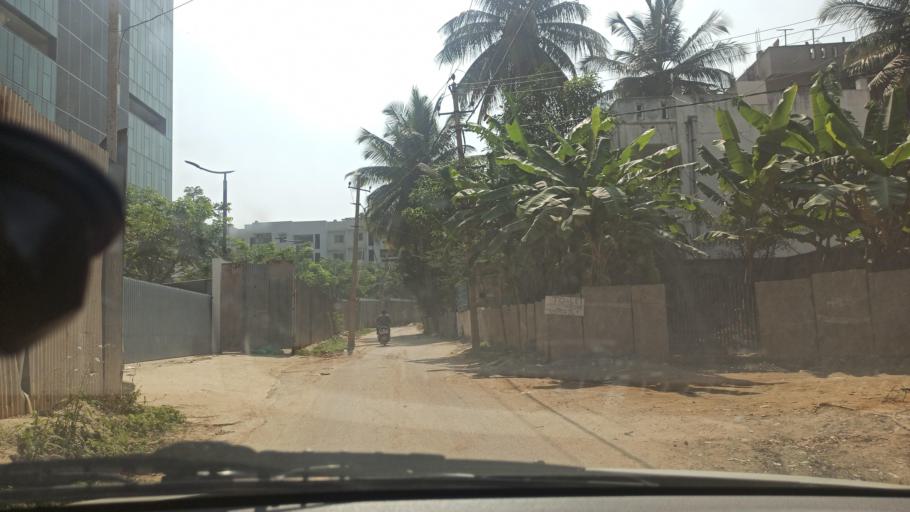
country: IN
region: Karnataka
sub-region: Bangalore Urban
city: Bangalore
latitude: 12.9370
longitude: 77.6881
